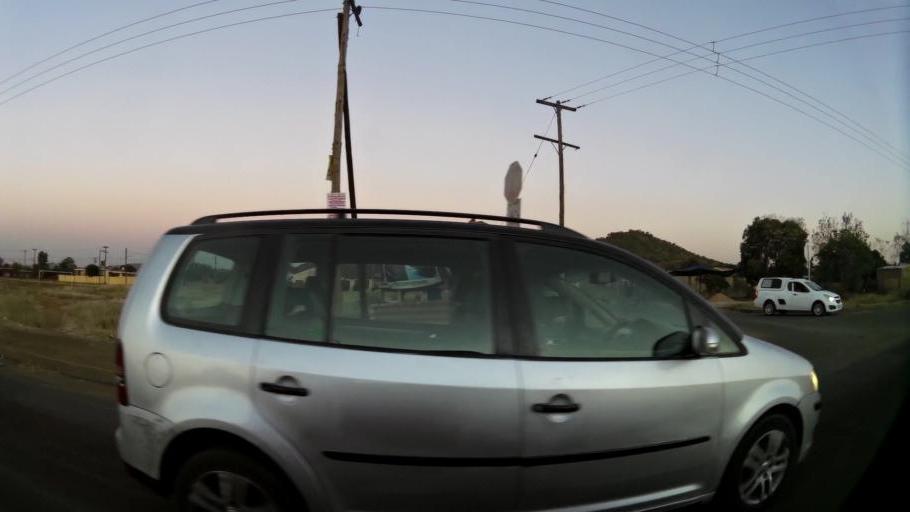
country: ZA
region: North-West
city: Ga-Rankuwa
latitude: -25.6013
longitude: 27.9730
